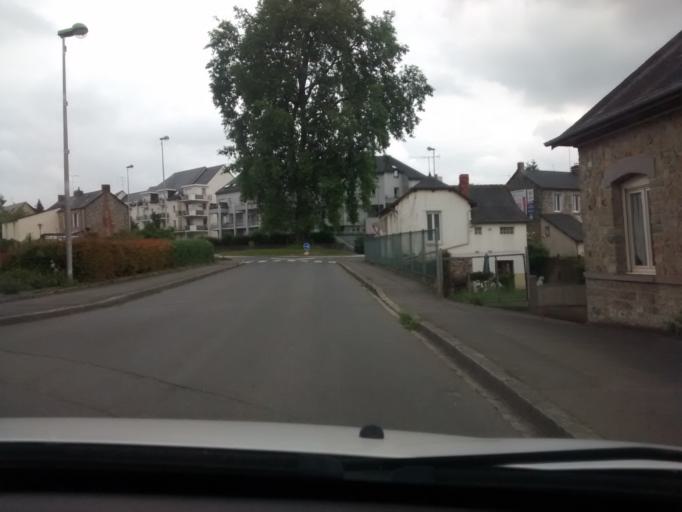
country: FR
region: Brittany
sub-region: Departement d'Ille-et-Vilaine
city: Liffre
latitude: 48.2120
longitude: -1.5088
